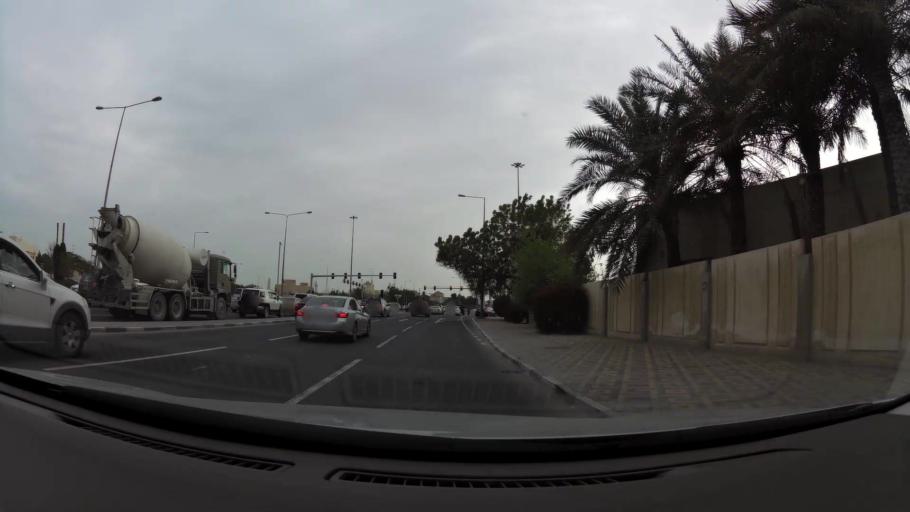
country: QA
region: Baladiyat ad Dawhah
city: Doha
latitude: 25.3294
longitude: 51.5053
